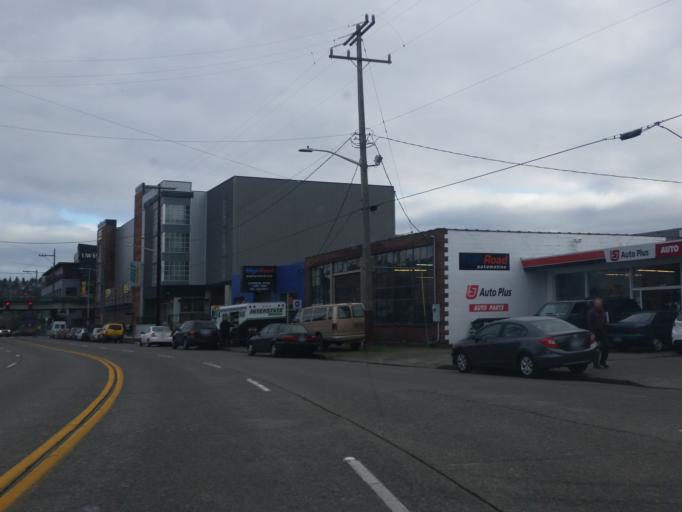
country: US
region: Washington
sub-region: King County
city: Seattle
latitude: 47.6637
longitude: -122.3784
